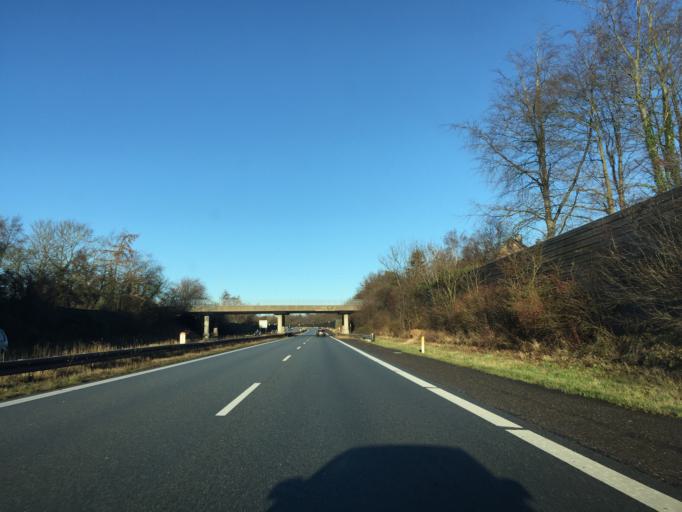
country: DK
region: South Denmark
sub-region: Nyborg Kommune
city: Nyborg
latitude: 55.3223
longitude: 10.8052
